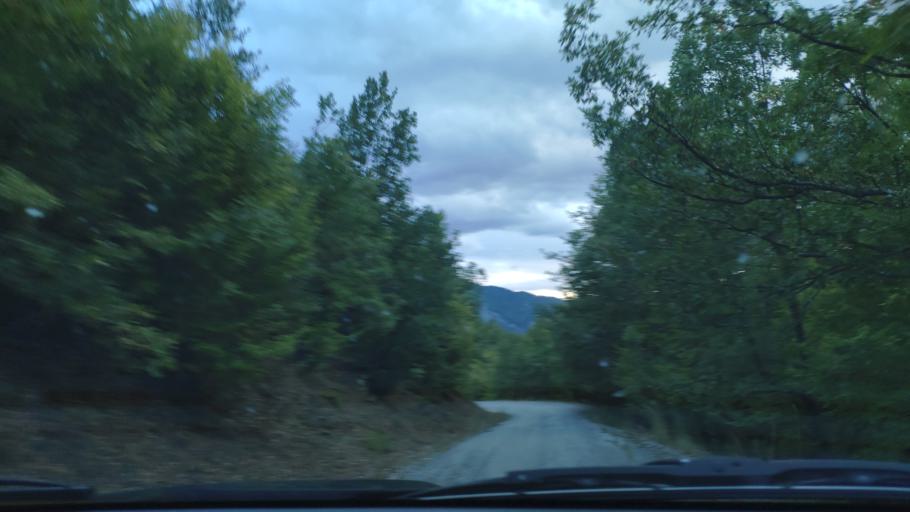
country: AL
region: Korce
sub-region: Rrethi i Kolonjes
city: Erseke
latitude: 40.2509
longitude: 20.8667
